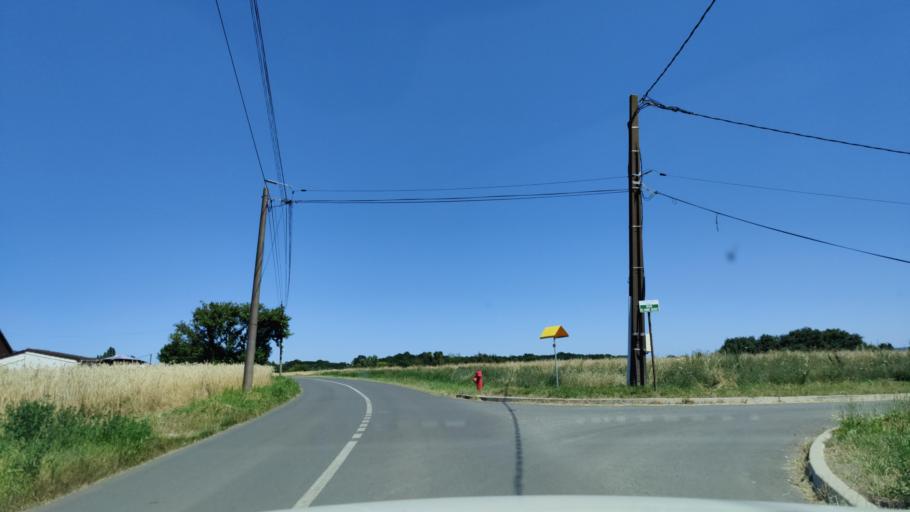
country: FR
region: Ile-de-France
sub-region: Departement de l'Essonne
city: Bruyeres-le-Chatel
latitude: 48.5956
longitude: 2.1686
